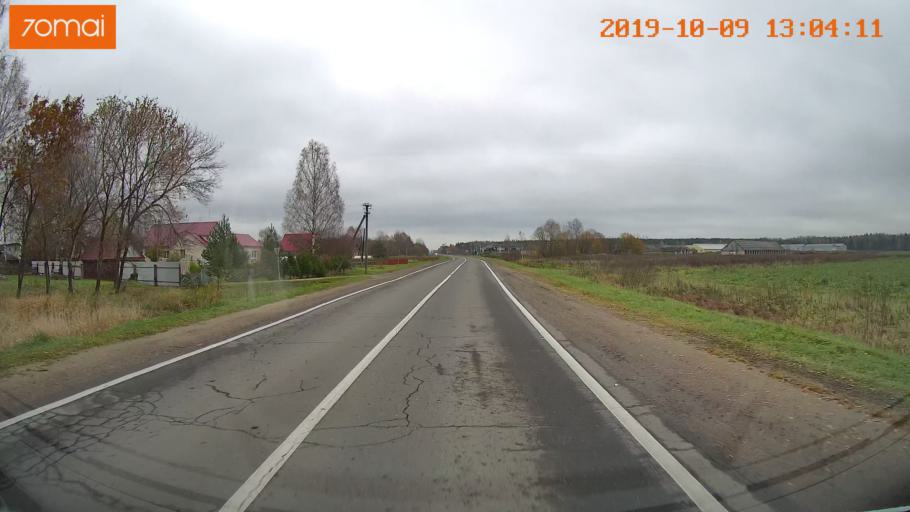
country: RU
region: Jaroslavl
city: Lyubim
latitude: 58.3586
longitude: 40.5476
